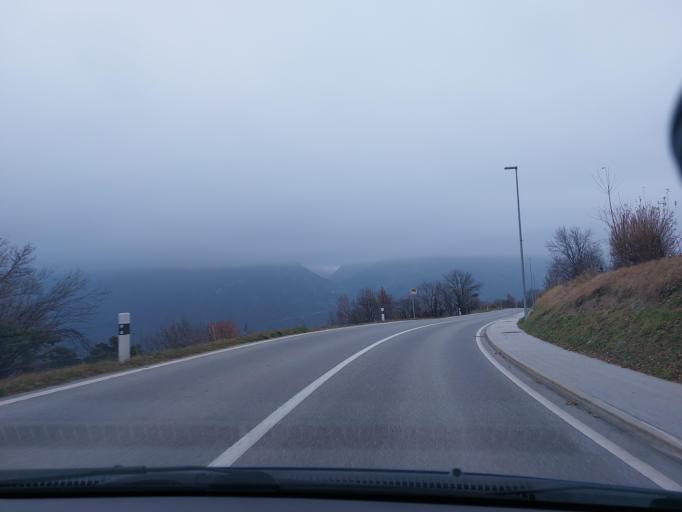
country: CH
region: Valais
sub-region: Sierre District
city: Veyras
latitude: 46.3147
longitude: 7.5281
